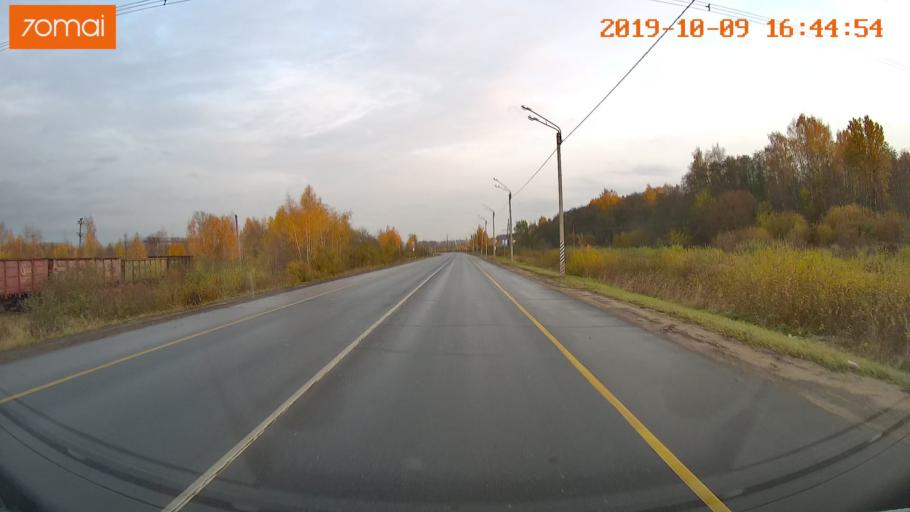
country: RU
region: Kostroma
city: Volgorechensk
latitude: 57.4495
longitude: 41.1471
